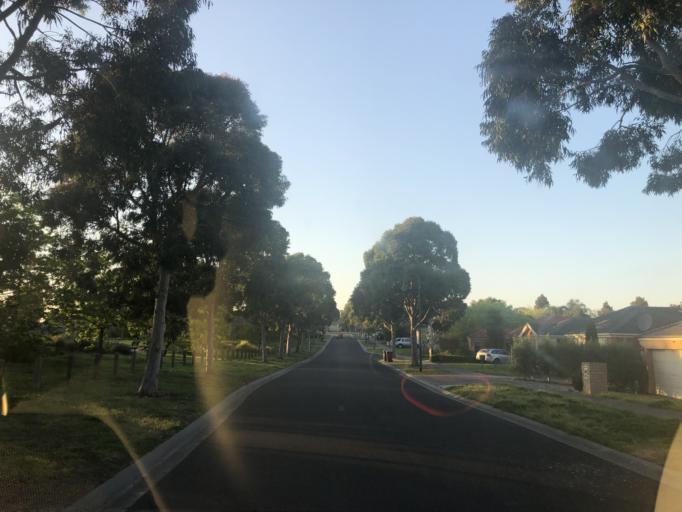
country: AU
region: Victoria
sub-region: Casey
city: Lynbrook
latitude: -38.0473
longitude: 145.2597
